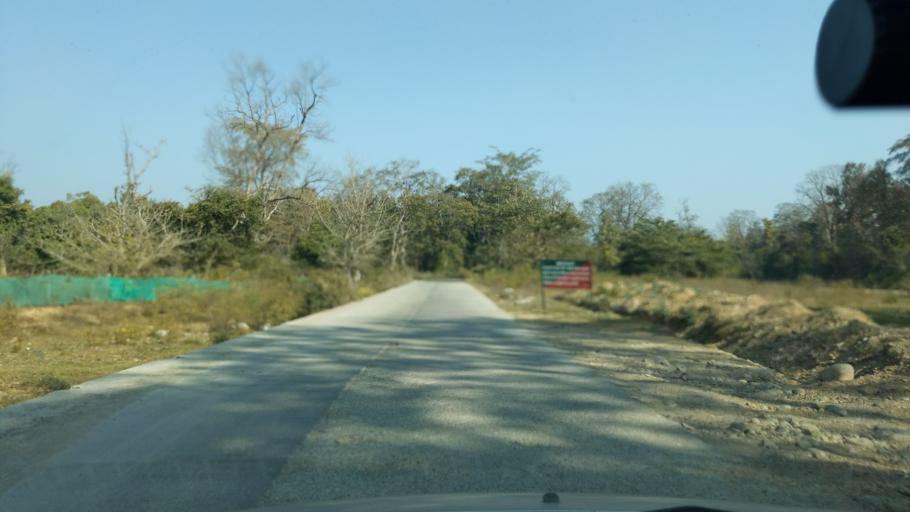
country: IN
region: Uttarakhand
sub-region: Naini Tal
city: Ramnagar
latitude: 29.4100
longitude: 79.1369
